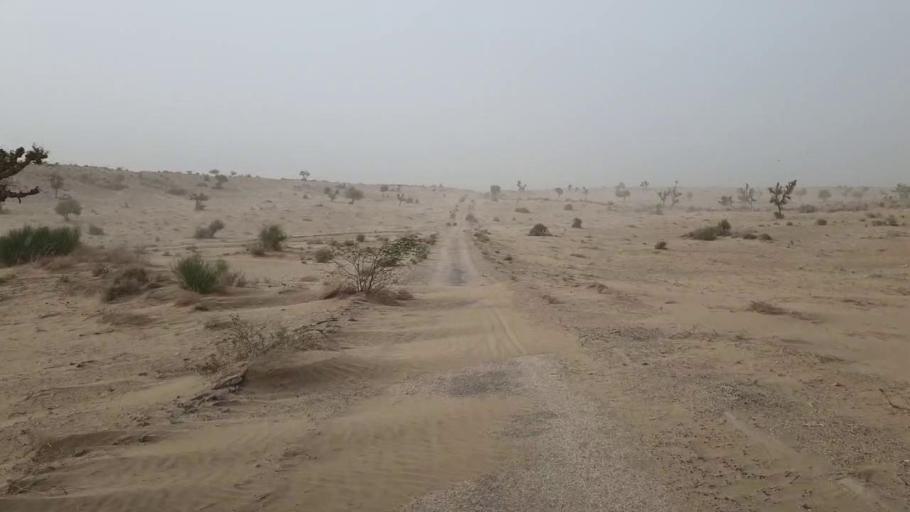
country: PK
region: Sindh
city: Islamkot
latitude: 24.5619
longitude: 70.3625
